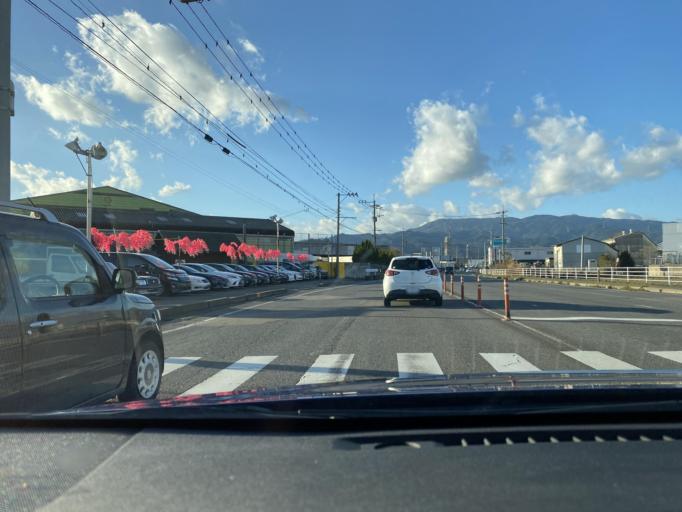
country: JP
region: Saga Prefecture
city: Tosu
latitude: 33.3581
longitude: 130.5095
